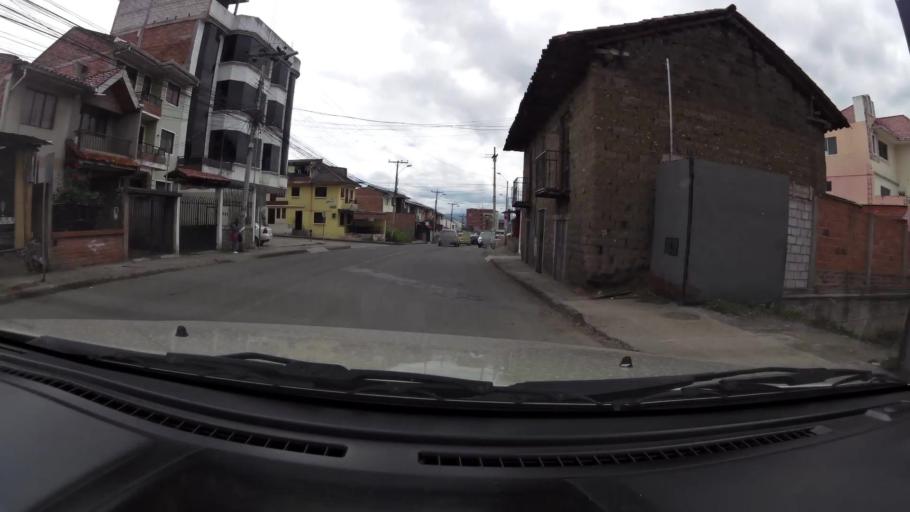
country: EC
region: Azuay
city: Cuenca
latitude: -2.8887
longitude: -79.0258
